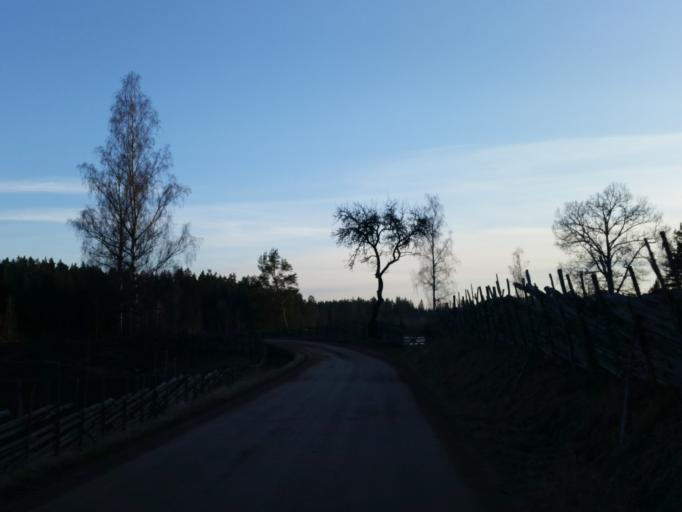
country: SE
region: Kalmar
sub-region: Oskarshamns Kommun
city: Oskarshamn
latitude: 57.3397
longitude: 16.4697
